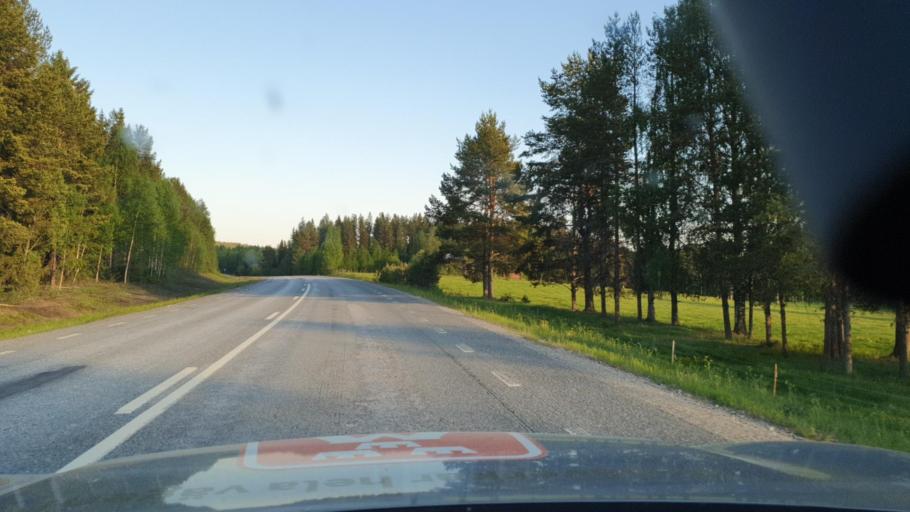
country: SE
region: Vaesternorrland
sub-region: Solleftea Kommun
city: As
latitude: 63.4192
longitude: 16.9555
